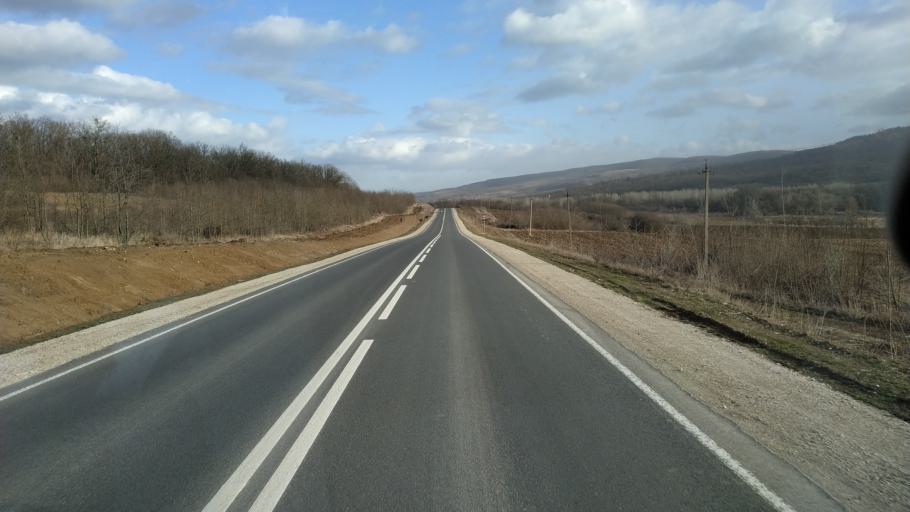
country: MD
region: Calarasi
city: Calarasi
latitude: 47.3102
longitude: 28.1248
